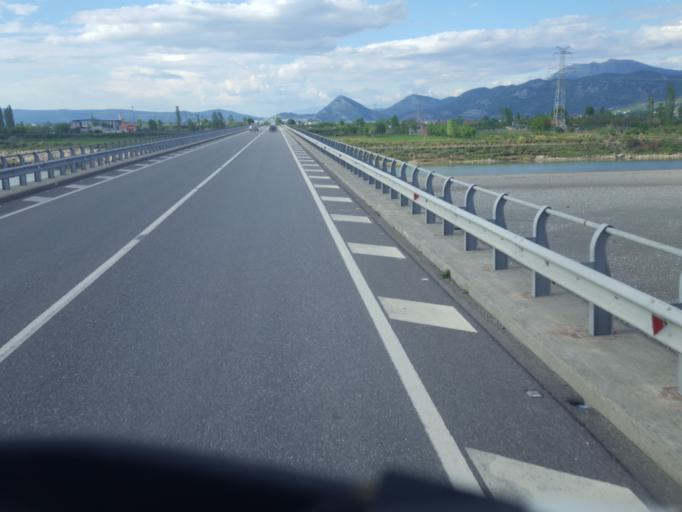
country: AL
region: Lezhe
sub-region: Rrethi i Lezhes
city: Shenkoll
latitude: 41.6843
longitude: 19.6720
